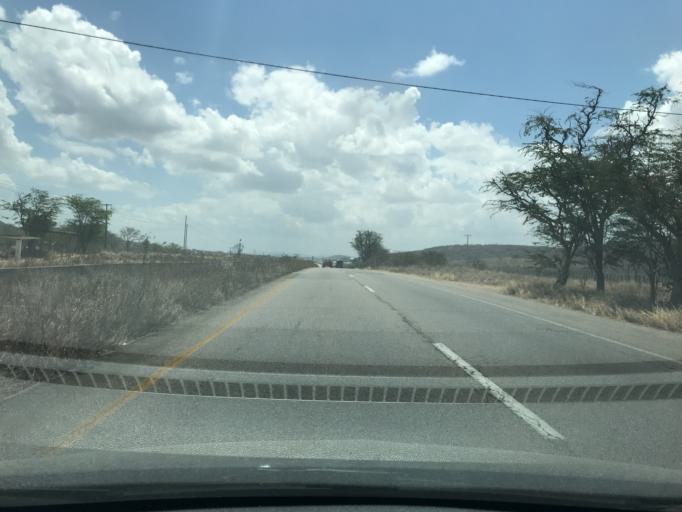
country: BR
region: Pernambuco
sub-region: Bezerros
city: Bezerros
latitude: -8.2967
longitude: -35.8689
